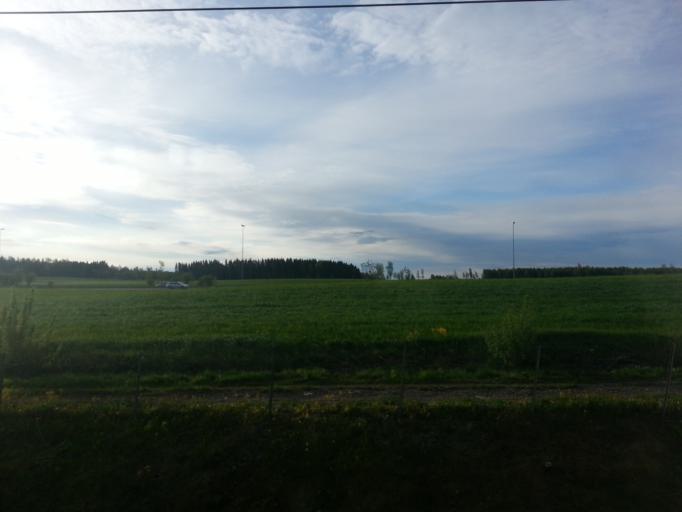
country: NO
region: Akershus
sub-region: Ullensaker
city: Jessheim
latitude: 60.1161
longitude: 11.1541
